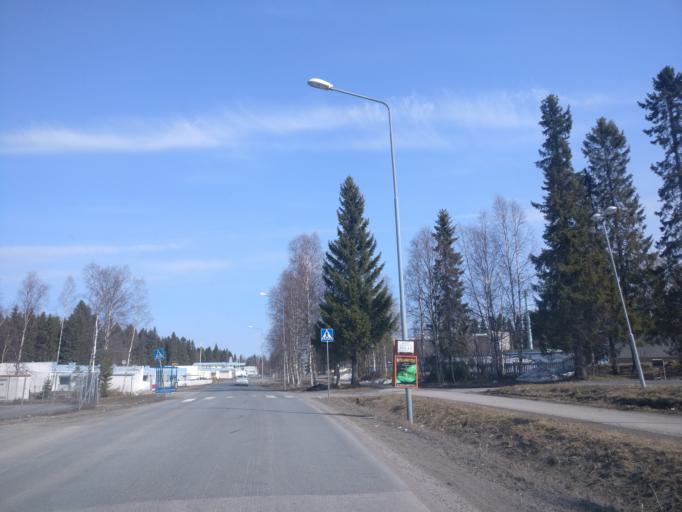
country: FI
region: Lapland
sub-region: Kemi-Tornio
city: Kemi
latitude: 65.7258
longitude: 24.6212
